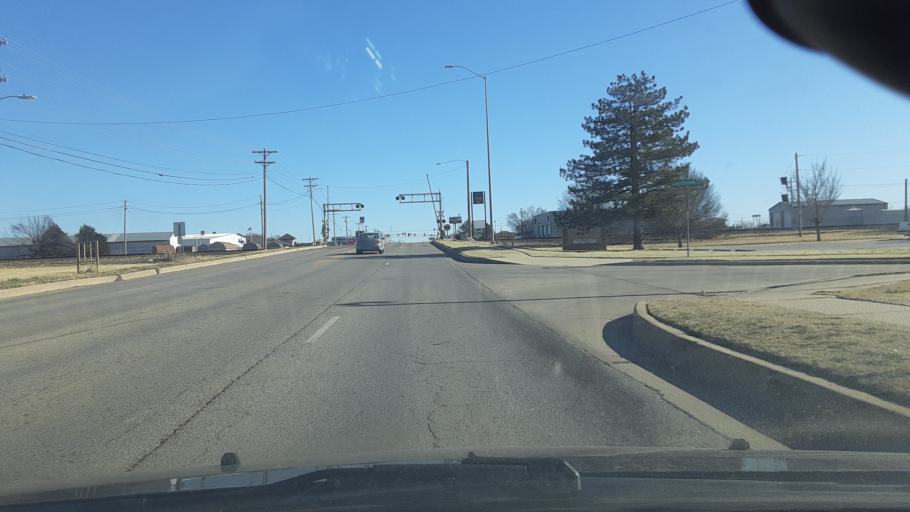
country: US
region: Oklahoma
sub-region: Kay County
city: Ponca City
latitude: 36.7386
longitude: -97.0782
